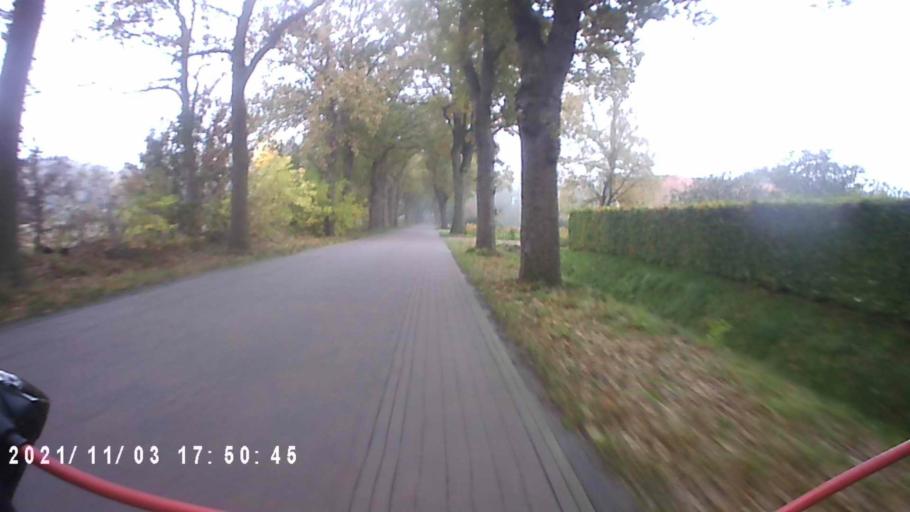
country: NL
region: Drenthe
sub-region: Gemeente Westerveld
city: Dwingeloo
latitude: 52.8428
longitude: 6.3143
